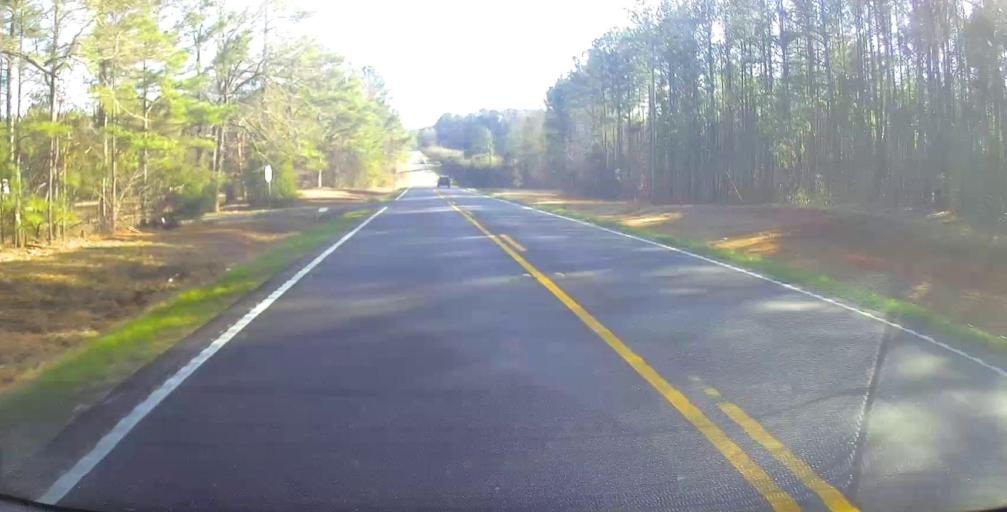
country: US
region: Georgia
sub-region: Talbot County
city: Sardis
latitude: 32.7894
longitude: -84.6928
